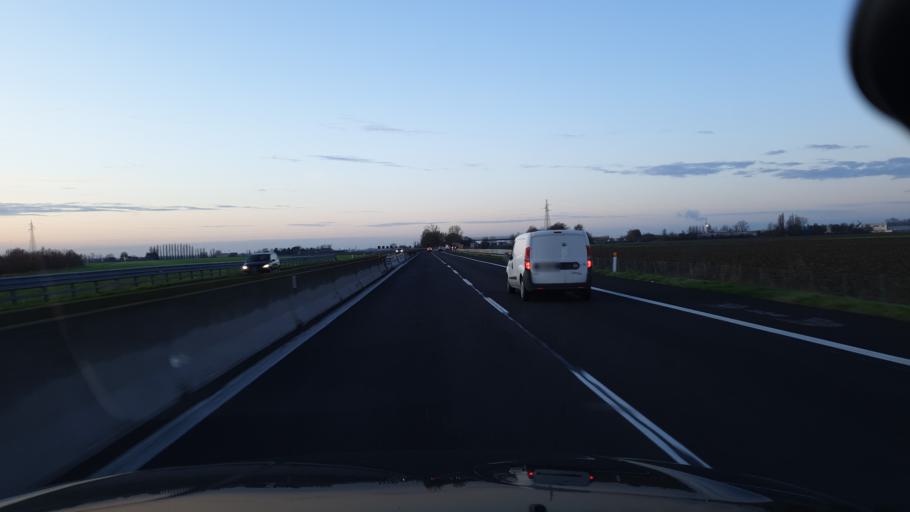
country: IT
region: Veneto
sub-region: Provincia di Rovigo
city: Fiesso Umbertiano
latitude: 44.9513
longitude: 11.6375
